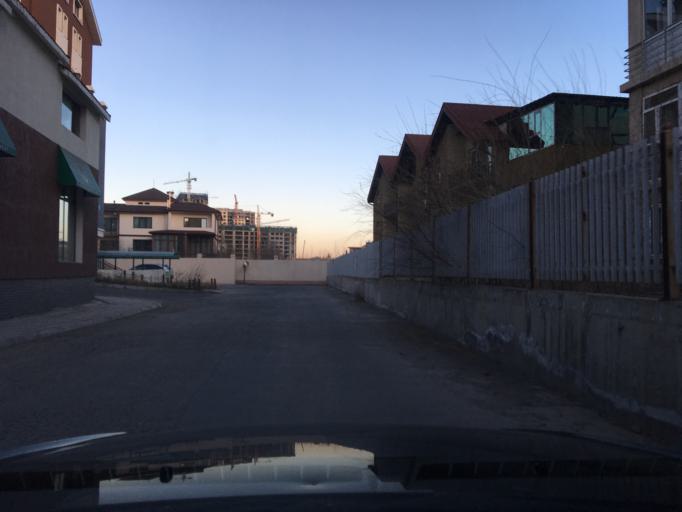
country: MN
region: Ulaanbaatar
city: Ulaanbaatar
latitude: 47.8937
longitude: 106.9203
